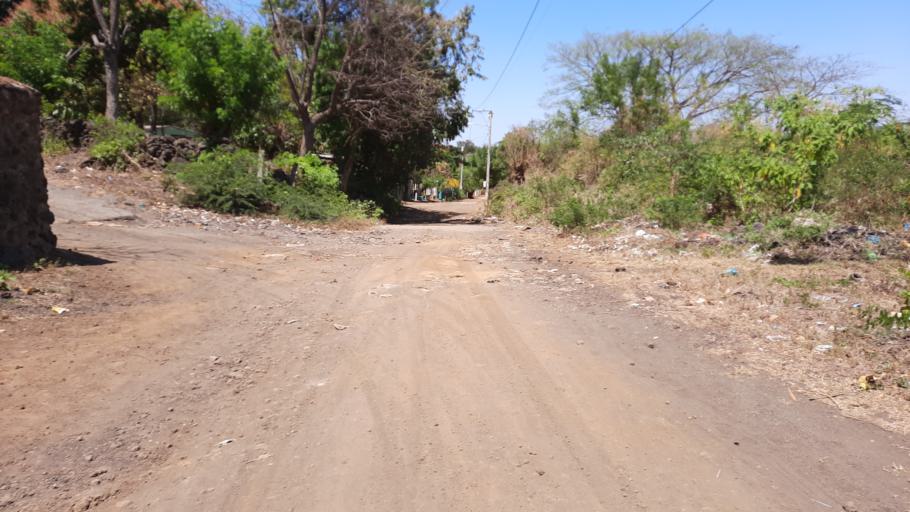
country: NI
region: Masaya
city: Ticuantepe
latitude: 12.0279
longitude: -86.1671
